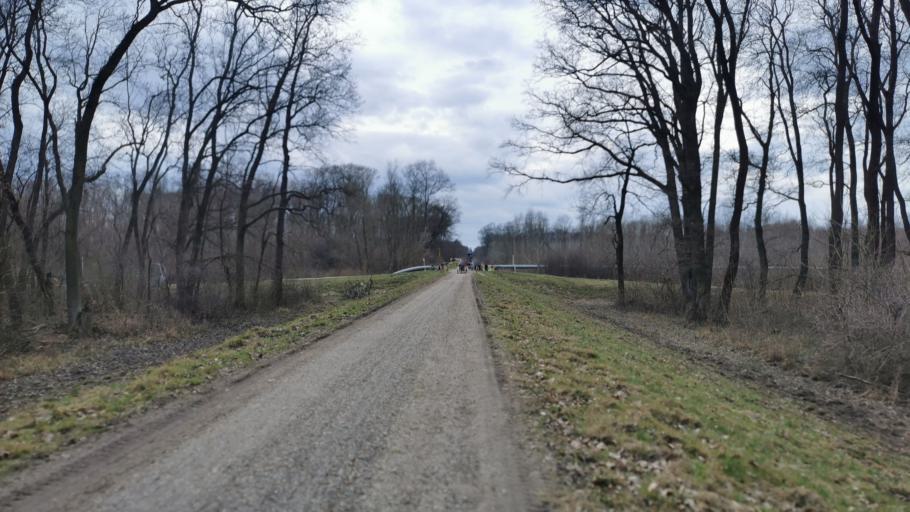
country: CZ
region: South Moravian
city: Rohatec
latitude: 48.8528
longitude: 17.1722
